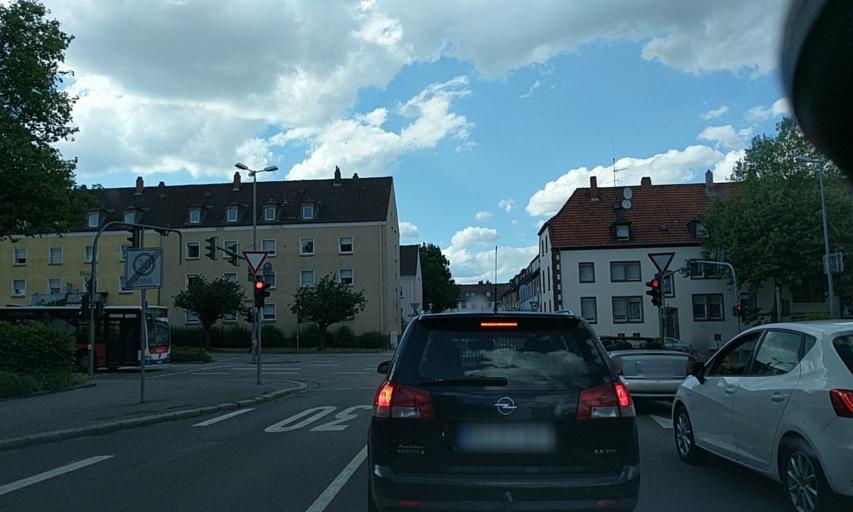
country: DE
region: Rheinland-Pfalz
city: Kaiserslautern
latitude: 49.4424
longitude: 7.7509
